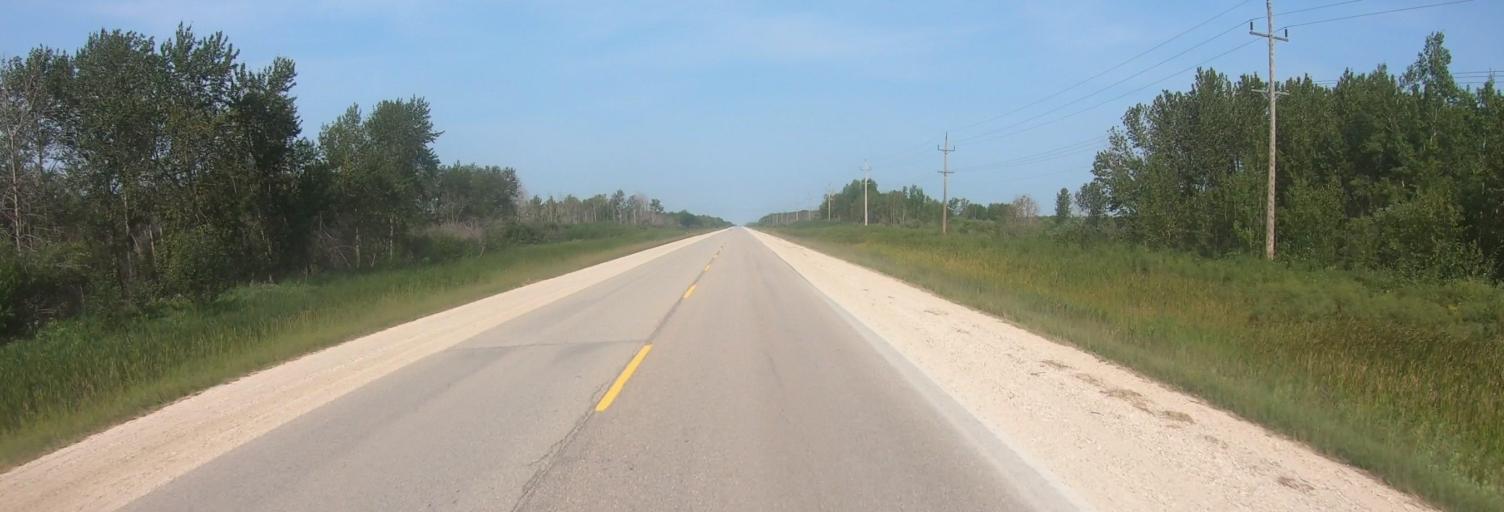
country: CA
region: Manitoba
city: La Broquerie
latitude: 49.2891
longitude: -96.5214
